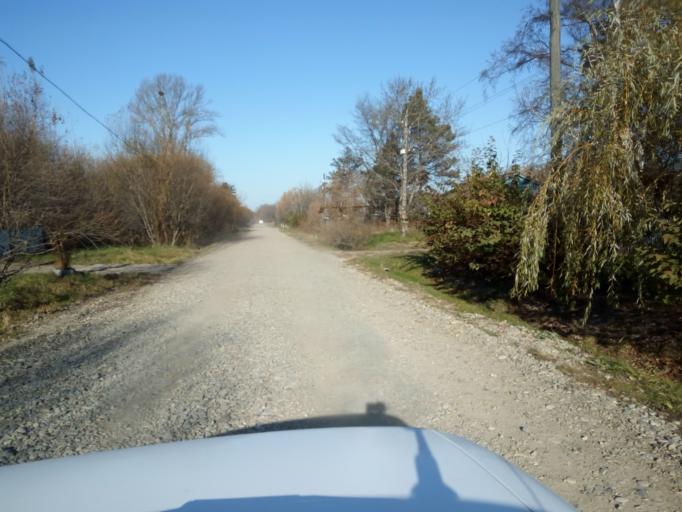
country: RU
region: Primorskiy
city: Lazo
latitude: 45.8776
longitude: 133.6553
